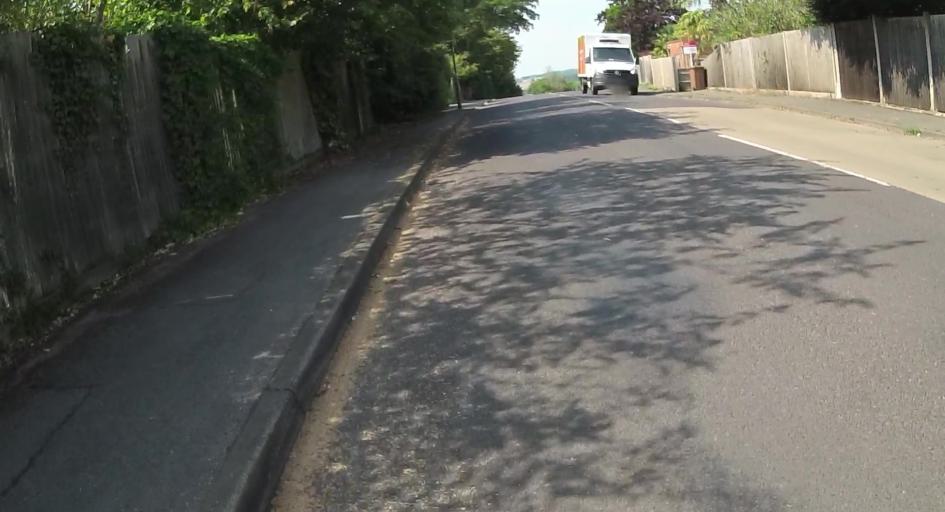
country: GB
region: England
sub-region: Surrey
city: Farnham
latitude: 51.1995
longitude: -0.8057
